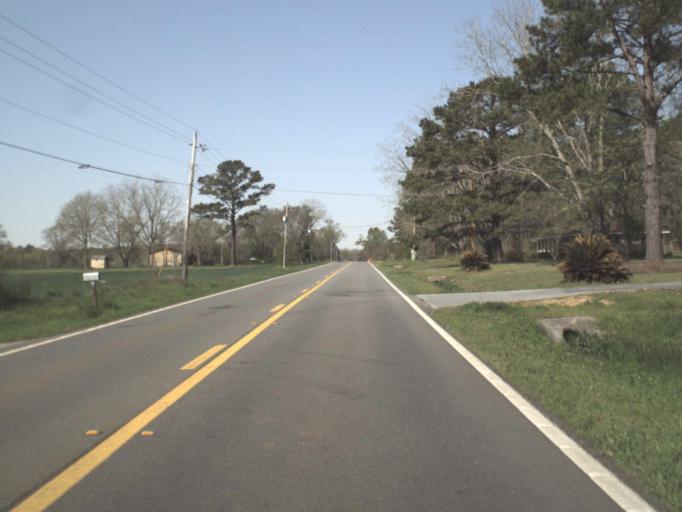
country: US
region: Florida
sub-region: Jackson County
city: Graceville
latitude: 30.9531
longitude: -85.4420
